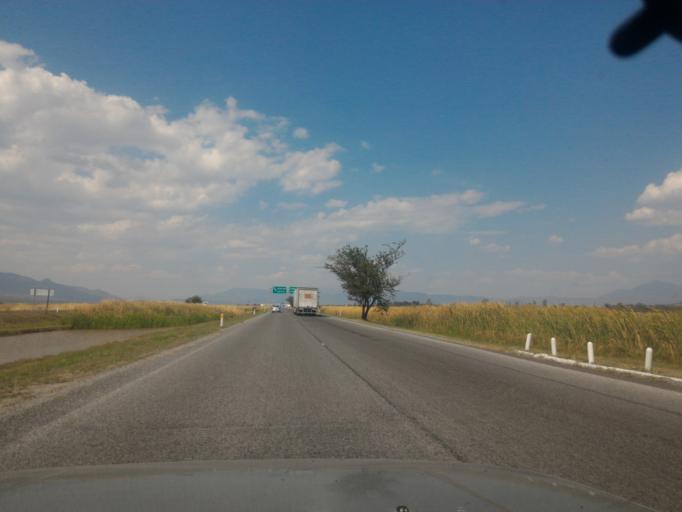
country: MX
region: Jalisco
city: Atoyac
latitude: 19.9992
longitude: -103.5356
